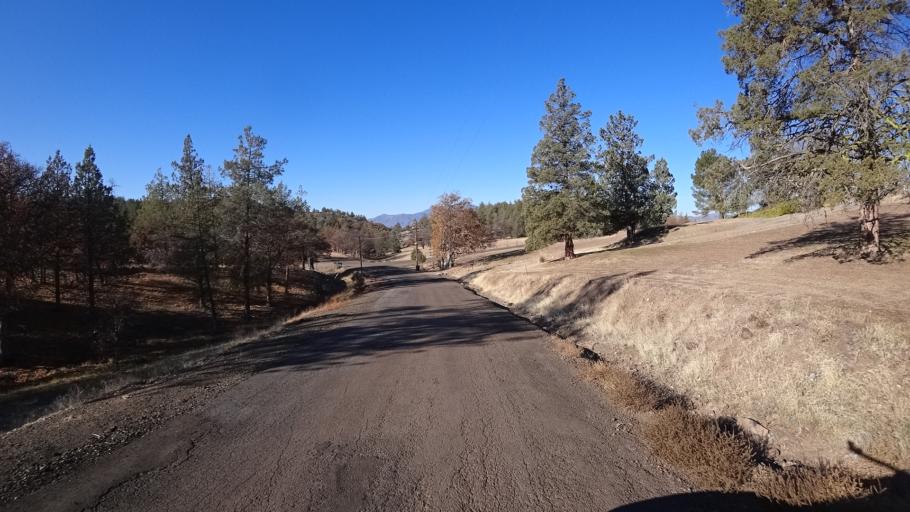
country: US
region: California
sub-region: Siskiyou County
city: Montague
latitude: 41.9131
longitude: -122.4313
